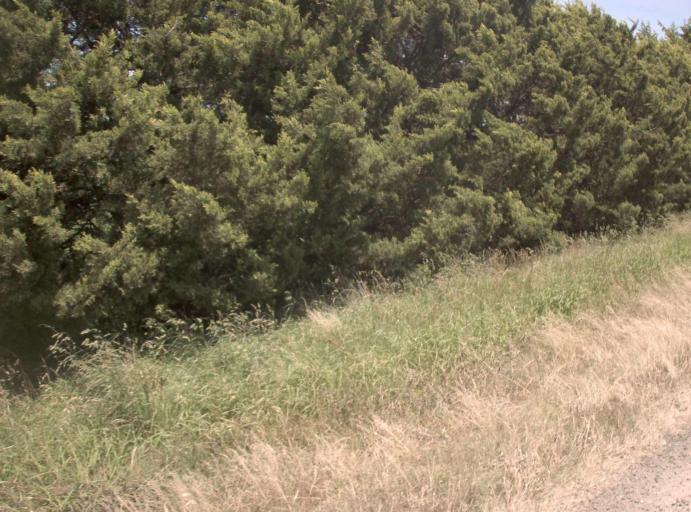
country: AU
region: Victoria
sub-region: Wellington
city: Heyfield
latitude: -38.0212
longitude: 146.8813
